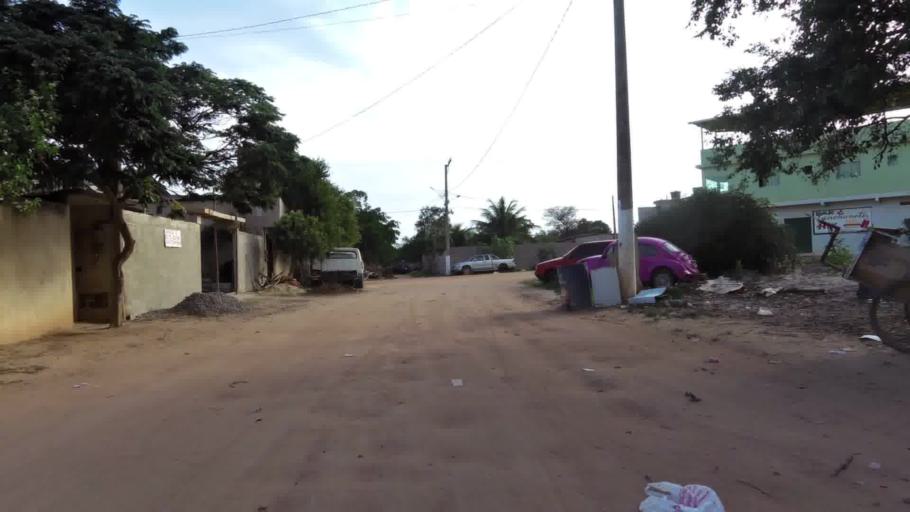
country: BR
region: Espirito Santo
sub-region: Piuma
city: Piuma
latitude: -20.8410
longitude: -40.7467
